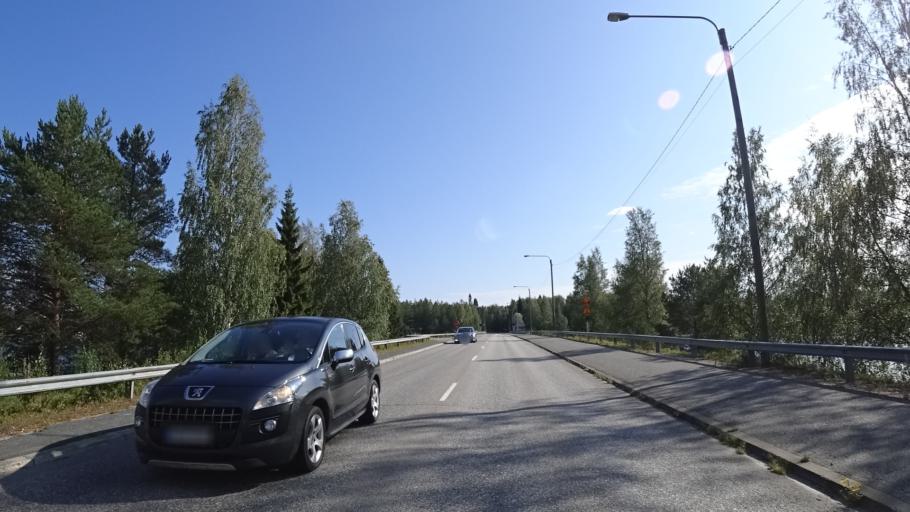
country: FI
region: North Karelia
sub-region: Joensuu
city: Eno
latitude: 62.8044
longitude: 30.1528
